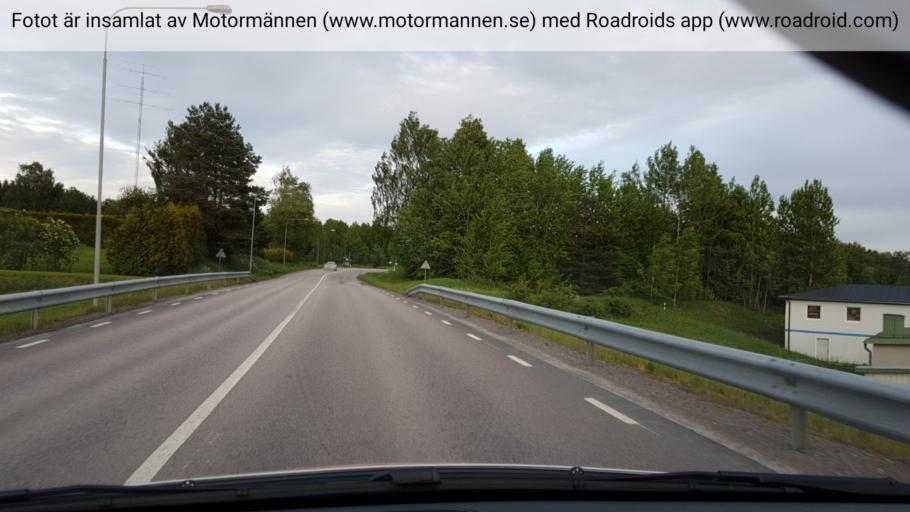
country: SE
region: Vaestmanland
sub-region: Kopings Kommun
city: Kolsva
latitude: 59.5872
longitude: 15.8614
